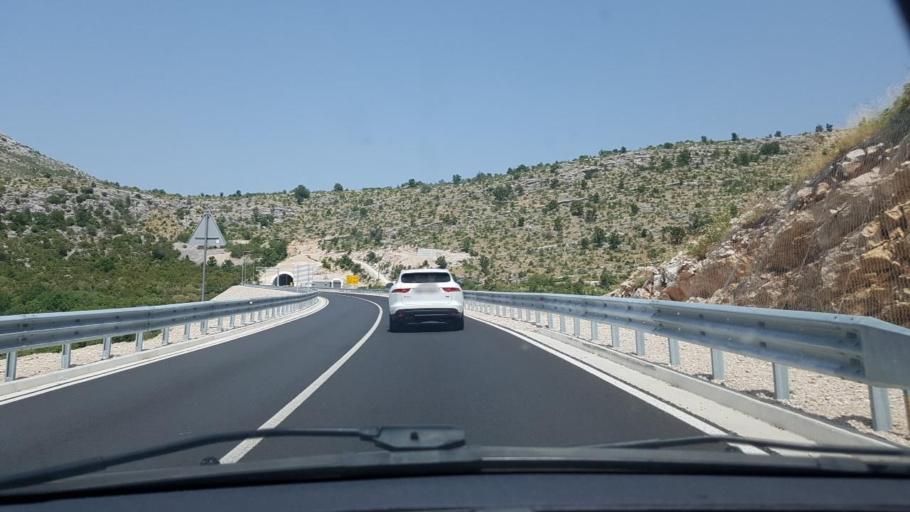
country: HR
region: Dubrovacko-Neretvanska
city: Podgora
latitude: 42.9510
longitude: 17.7839
